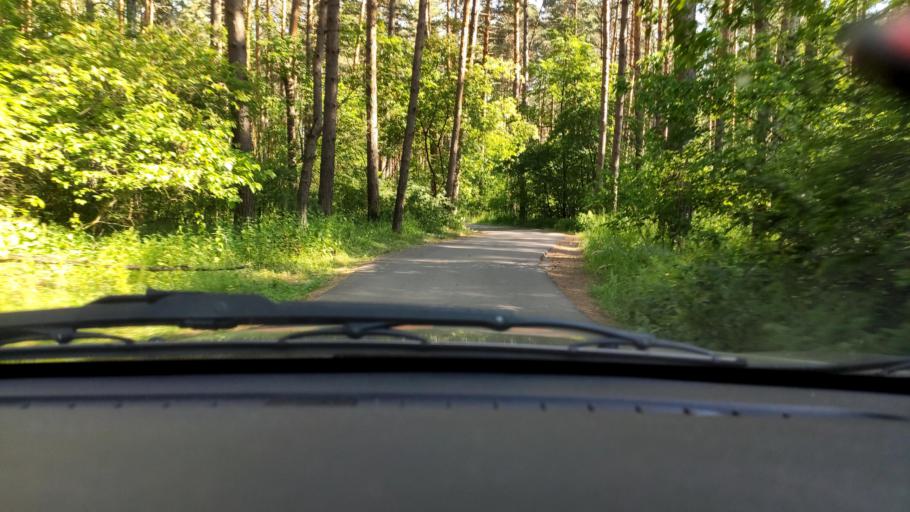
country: RU
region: Voronezj
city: Somovo
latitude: 51.7988
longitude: 39.3803
